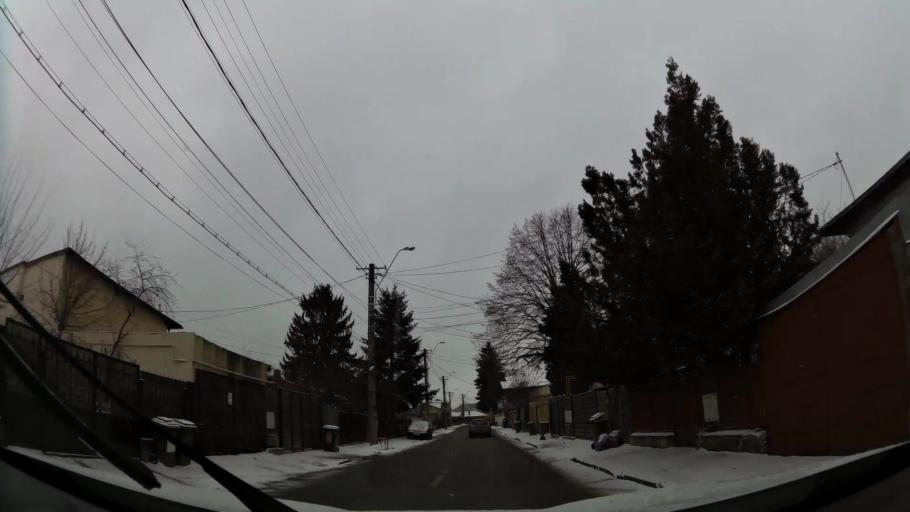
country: RO
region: Prahova
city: Ploiesti
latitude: 44.9304
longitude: 26.0157
